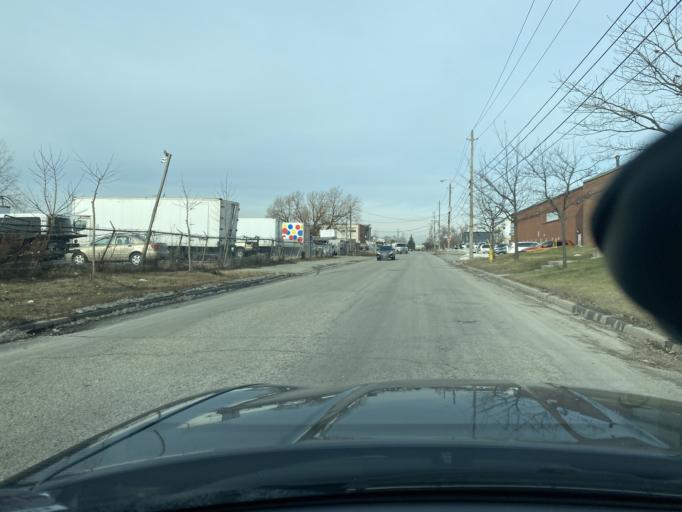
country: CA
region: Ontario
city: Scarborough
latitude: 43.7231
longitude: -79.2821
